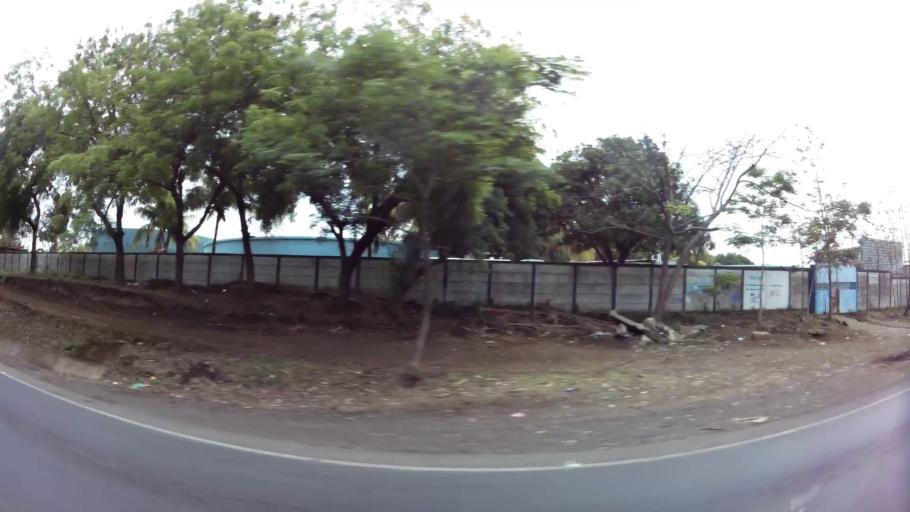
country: NI
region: Masaya
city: Masaya
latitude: 11.9639
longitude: -86.0825
